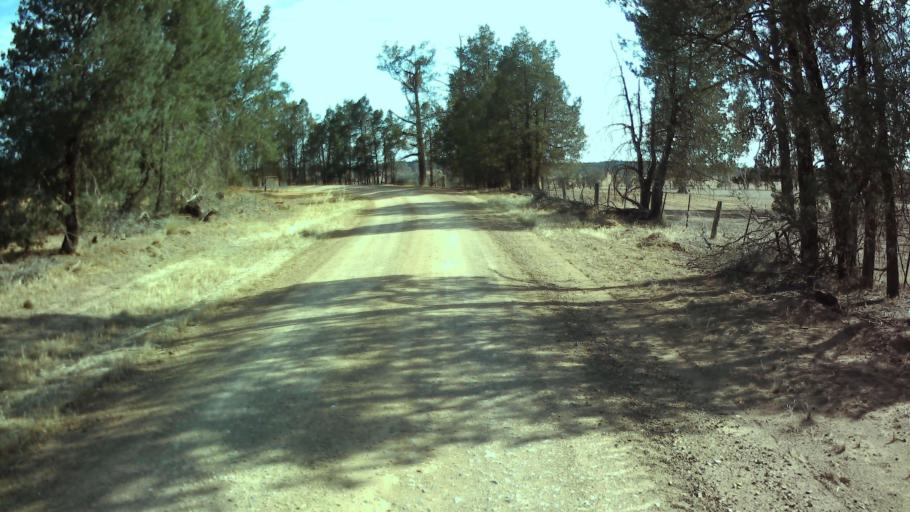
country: AU
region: New South Wales
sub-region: Weddin
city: Grenfell
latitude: -33.7687
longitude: 148.0474
